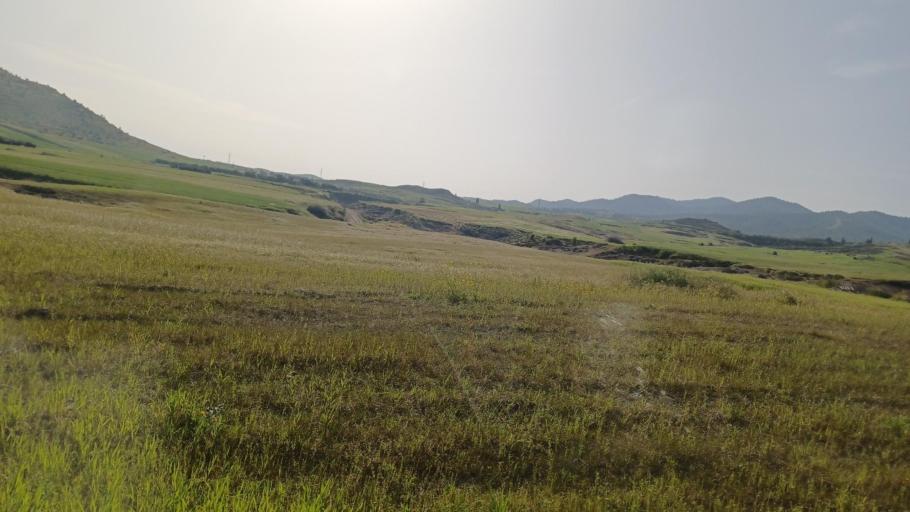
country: CY
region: Lefkosia
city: Lefka
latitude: 35.0902
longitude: 32.9440
